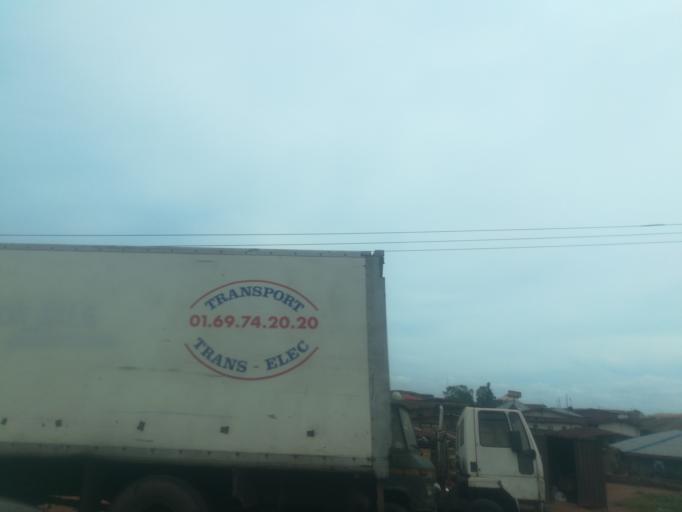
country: NG
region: Oyo
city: Ibadan
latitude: 7.3720
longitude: 3.9297
